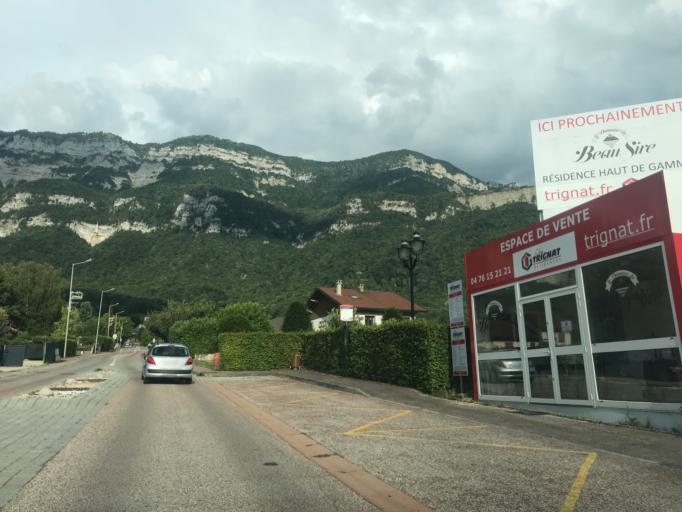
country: FR
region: Rhone-Alpes
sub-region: Departement de la Savoie
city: Mery
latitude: 45.6426
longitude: 5.9291
